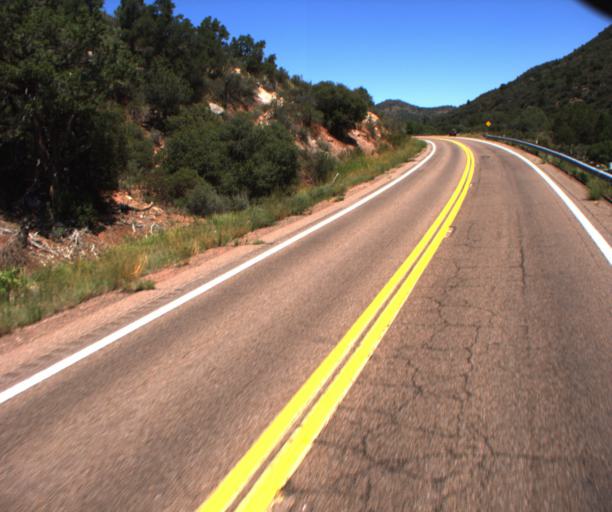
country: US
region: Arizona
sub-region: Navajo County
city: Cibecue
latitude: 33.8738
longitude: -110.3985
